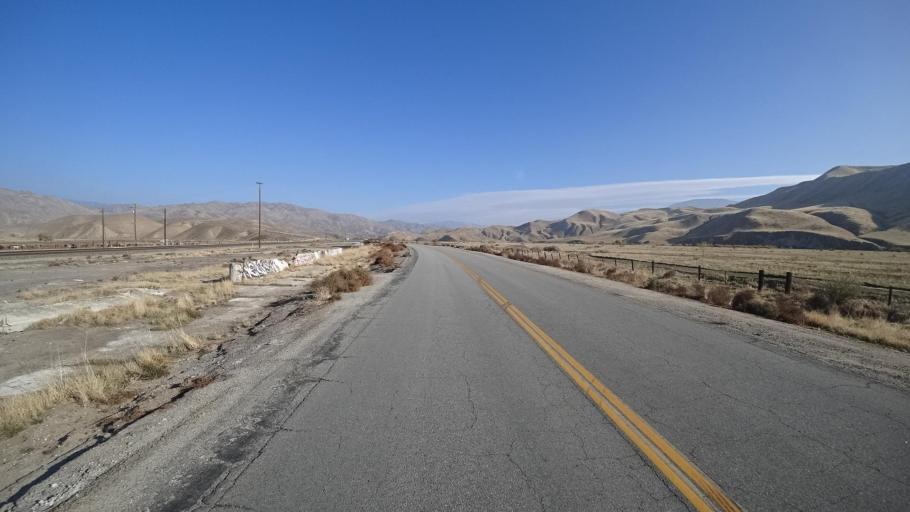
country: US
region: California
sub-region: Kern County
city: Arvin
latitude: 35.3262
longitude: -118.7397
